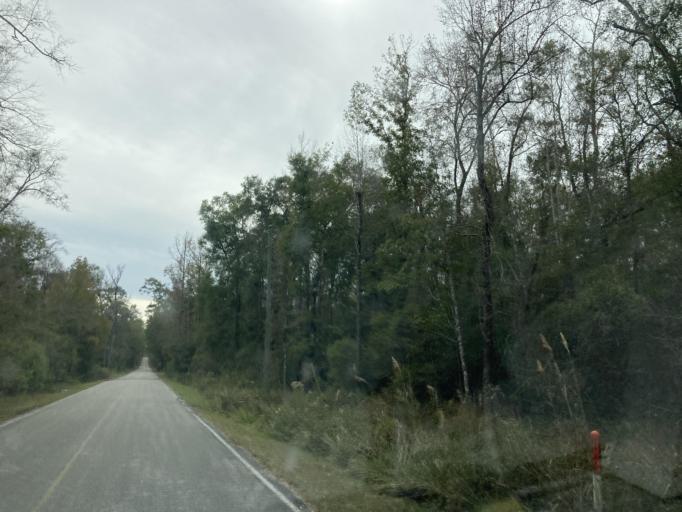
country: US
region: Mississippi
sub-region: Lamar County
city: Lumberton
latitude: 31.0622
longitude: -89.4336
